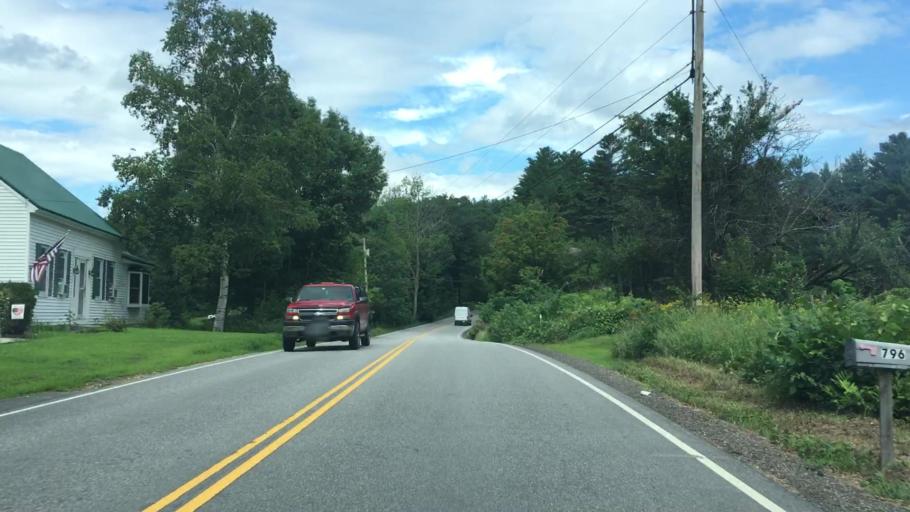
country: US
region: New Hampshire
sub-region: Belknap County
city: Laconia
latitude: 43.5807
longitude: -71.5127
